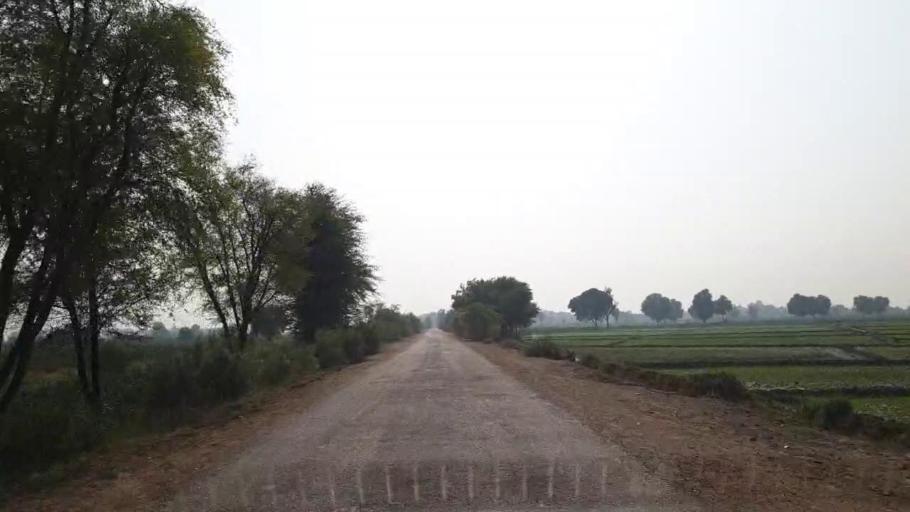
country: PK
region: Sindh
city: Sehwan
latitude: 26.4713
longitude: 67.7752
